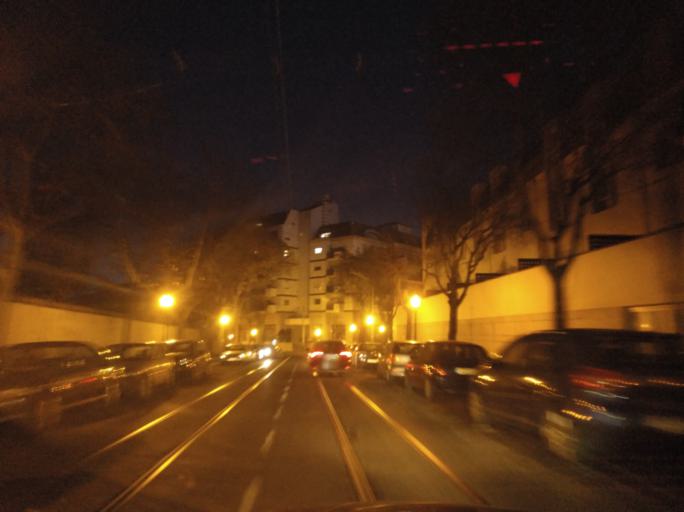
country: PT
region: Setubal
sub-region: Almada
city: Pragal
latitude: 38.7049
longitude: -9.1873
